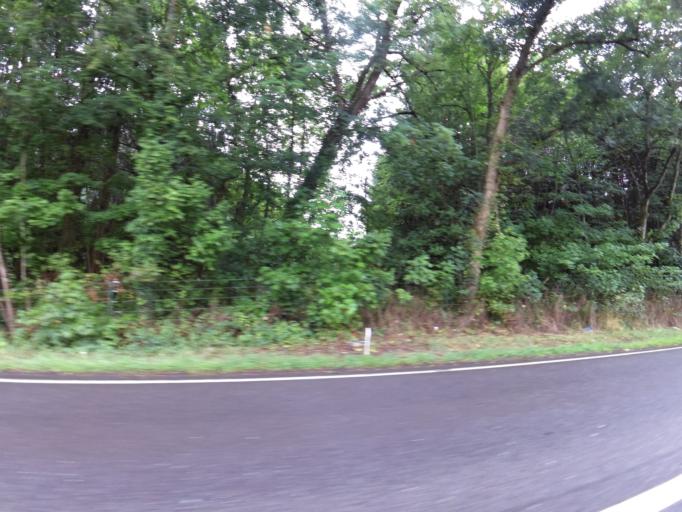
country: BE
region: Wallonia
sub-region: Province de Namur
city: Rochefort
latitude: 50.1459
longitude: 5.2200
